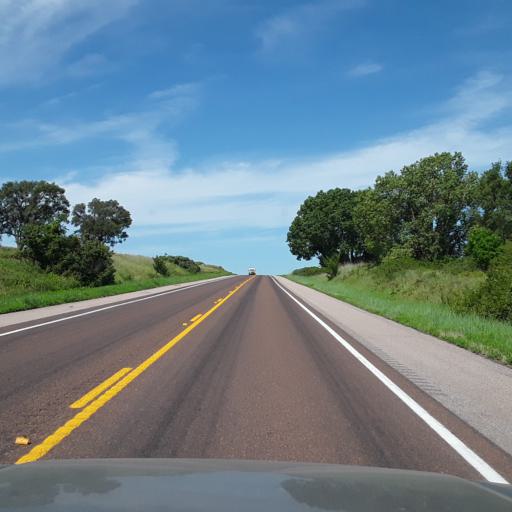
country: US
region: Nebraska
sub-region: Seward County
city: Milford
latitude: 40.8865
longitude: -96.9168
